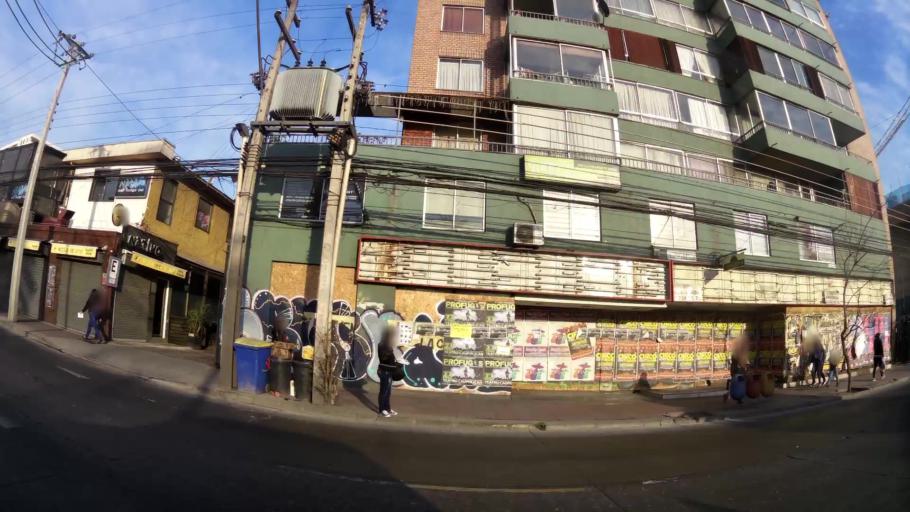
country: CL
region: Santiago Metropolitan
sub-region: Provincia de Santiago
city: Santiago
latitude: -33.4971
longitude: -70.6532
